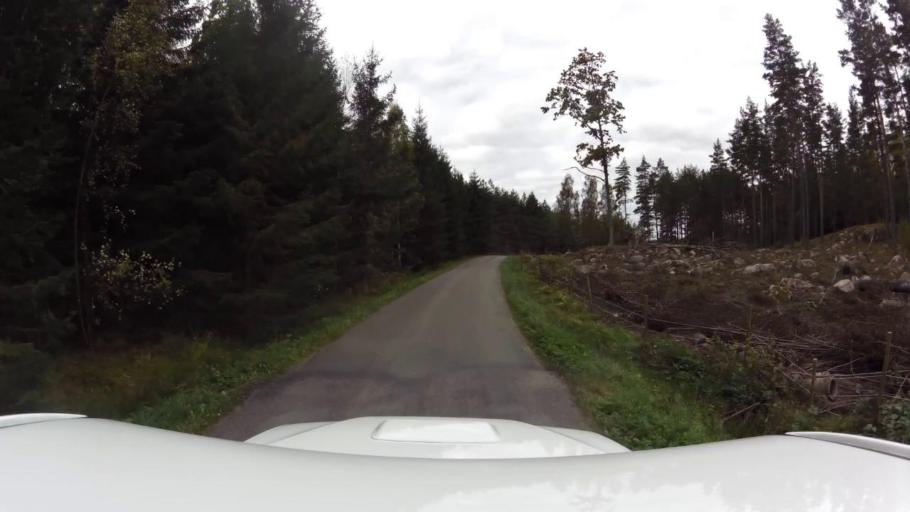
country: SE
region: OEstergoetland
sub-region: Kinda Kommun
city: Rimforsa
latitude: 58.1958
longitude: 15.5821
